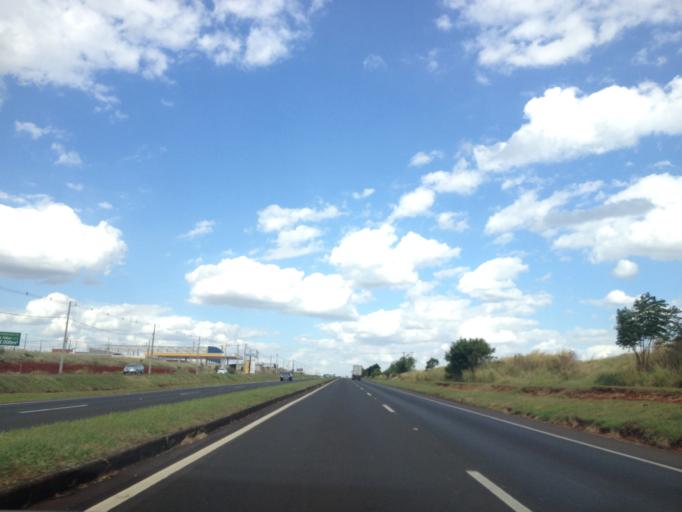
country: BR
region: Parana
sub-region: Marialva
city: Marialva
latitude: -23.4940
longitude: -51.8120
